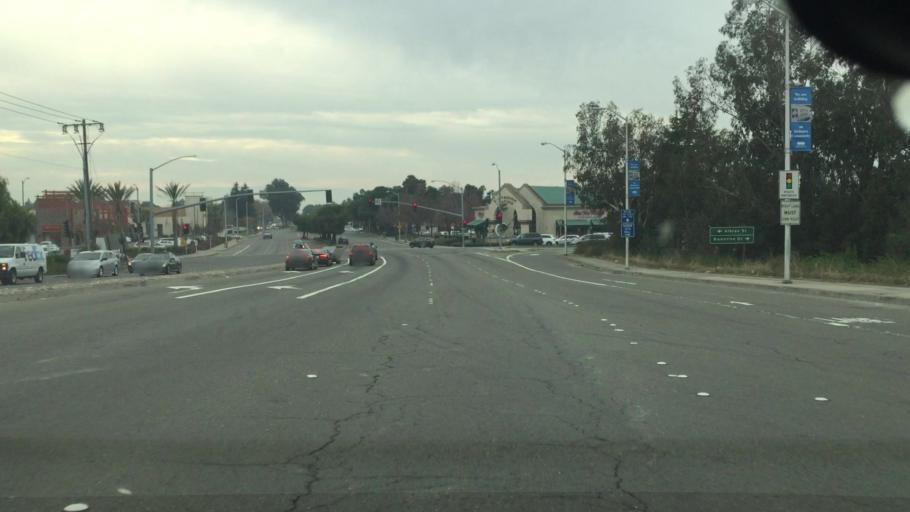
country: US
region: California
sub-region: Alameda County
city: Fremont
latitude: 37.5213
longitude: -121.9888
